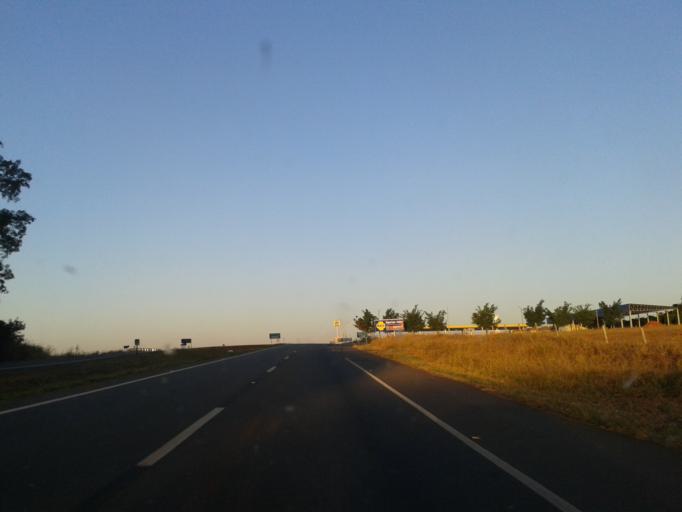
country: BR
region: Goias
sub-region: Itaberai
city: Itaberai
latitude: -16.0192
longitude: -49.8558
